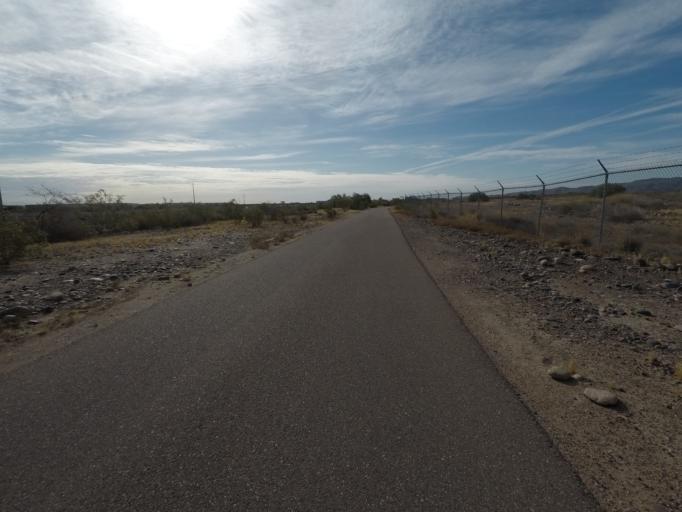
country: US
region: Arizona
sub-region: Maricopa County
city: Phoenix
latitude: 33.4193
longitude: -112.0569
